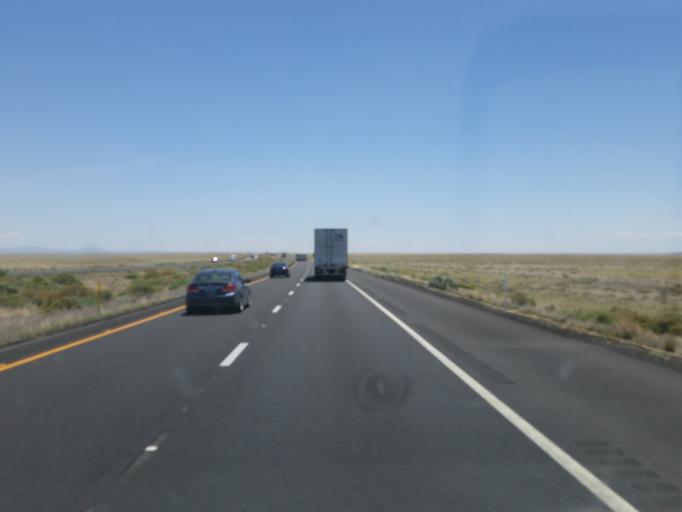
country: US
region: Arizona
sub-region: Coconino County
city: LeChee
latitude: 35.1209
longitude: -111.1575
